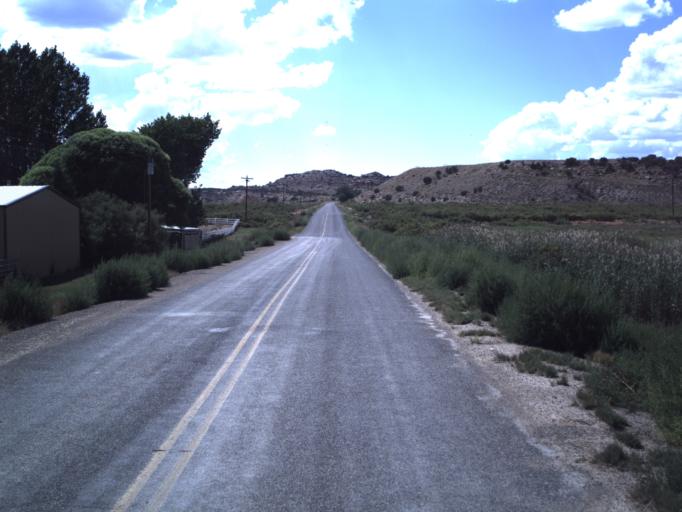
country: US
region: Utah
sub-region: Duchesne County
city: Duchesne
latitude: 40.1738
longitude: -110.4296
